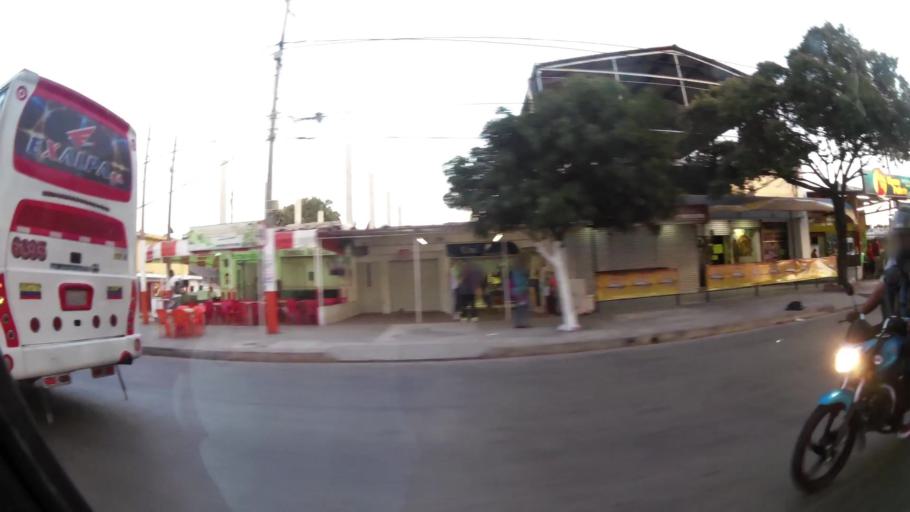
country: CO
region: Atlantico
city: Soledad
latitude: 10.9396
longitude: -74.7787
